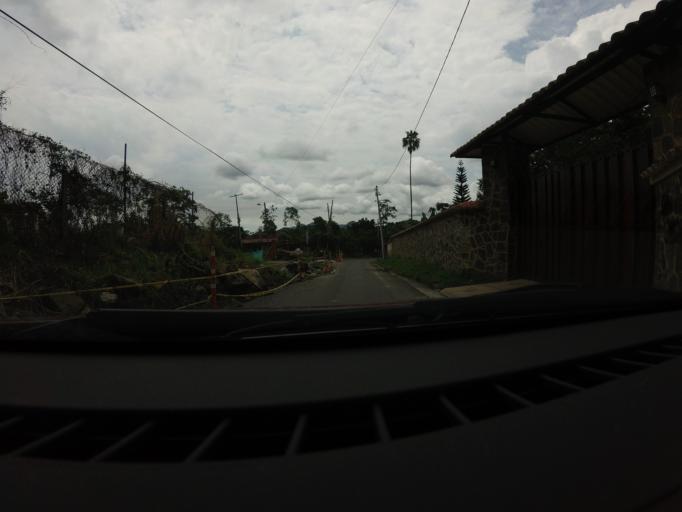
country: CO
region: Cundinamarca
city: La Vega
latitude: 4.9845
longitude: -74.3266
